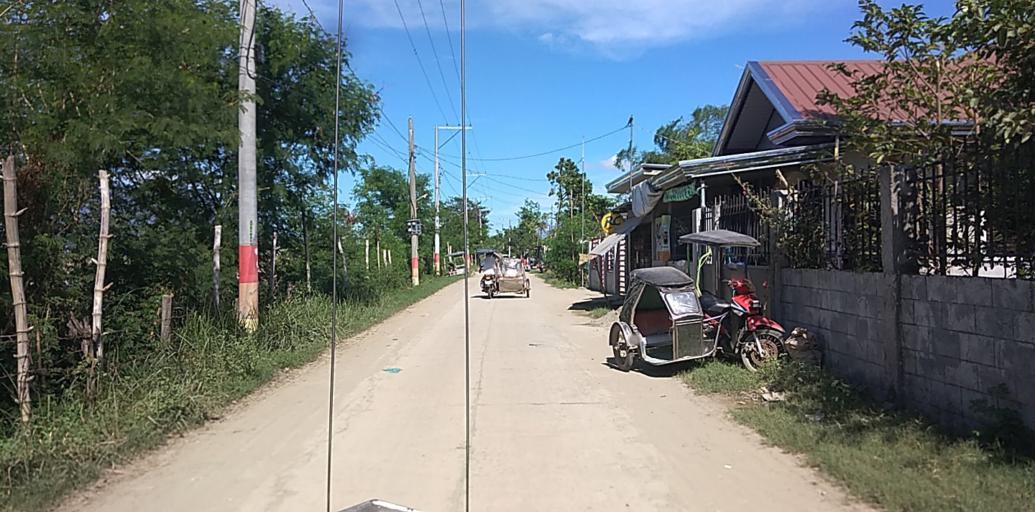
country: PH
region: Central Luzon
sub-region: Province of Pampanga
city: Candaba
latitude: 15.1200
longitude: 120.8135
